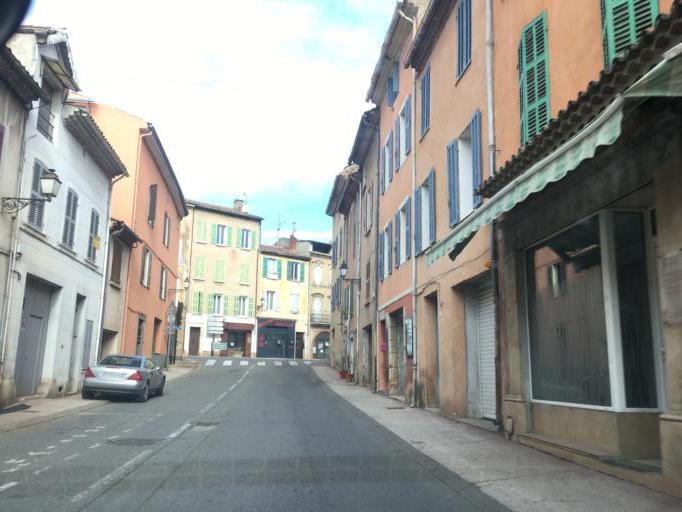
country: FR
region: Provence-Alpes-Cote d'Azur
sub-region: Departement du Var
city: Carces
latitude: 43.4765
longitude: 6.1848
